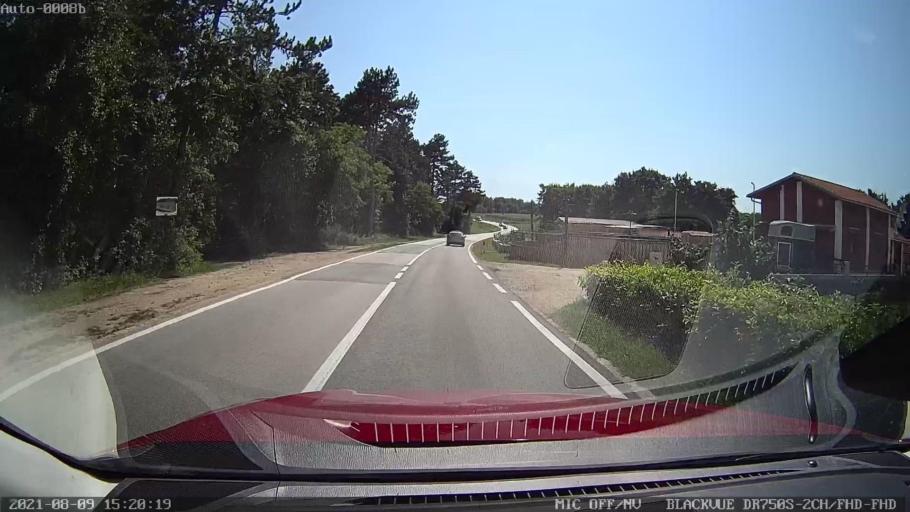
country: HR
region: Istarska
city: Pazin
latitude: 45.2075
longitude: 13.8993
